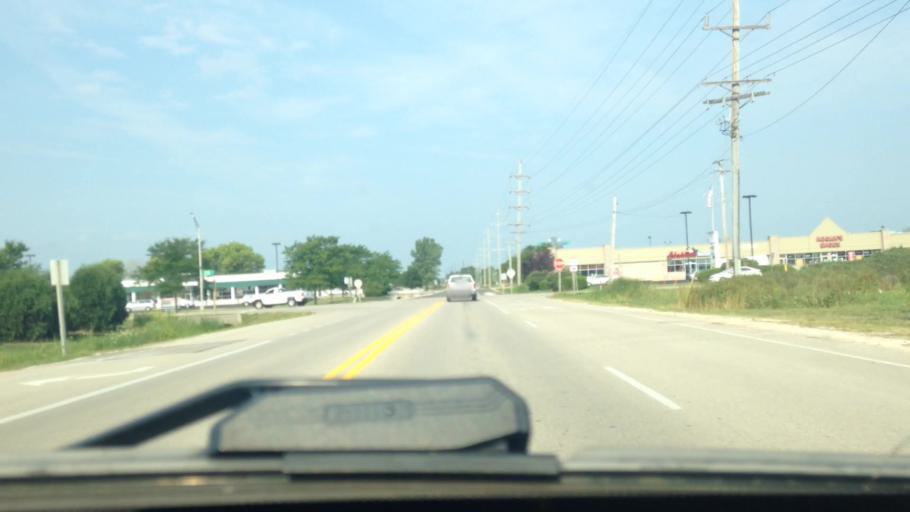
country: US
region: Wisconsin
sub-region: Fond du Lac County
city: North Fond du Lac
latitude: 43.7917
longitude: -88.4856
